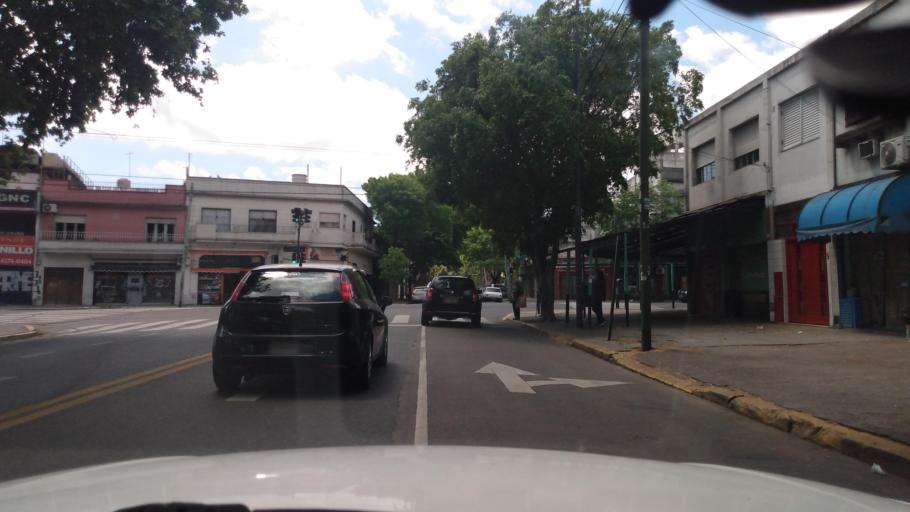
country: AR
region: Buenos Aires
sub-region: Partido de General San Martin
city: General San Martin
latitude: -34.5738
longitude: -58.5033
